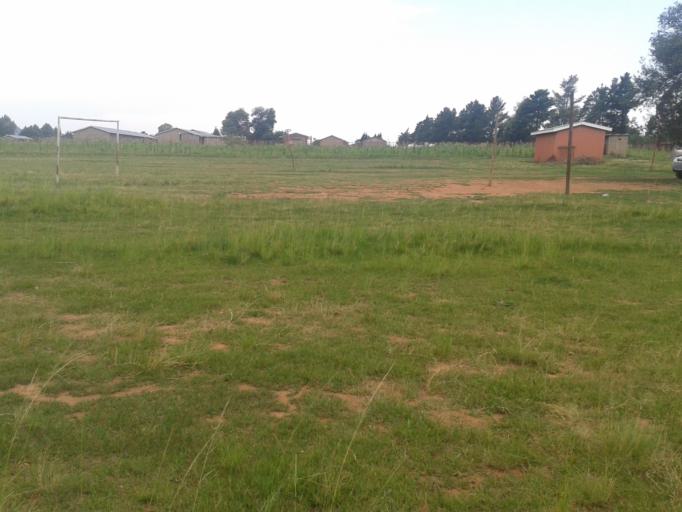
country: LS
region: Maseru
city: Maseru
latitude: -29.3716
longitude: 27.5062
